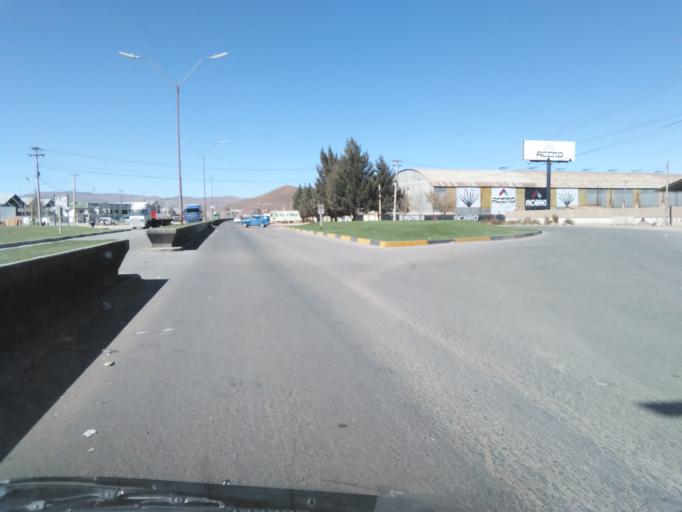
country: BO
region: Oruro
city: Oruro
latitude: -17.9773
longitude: -67.0616
